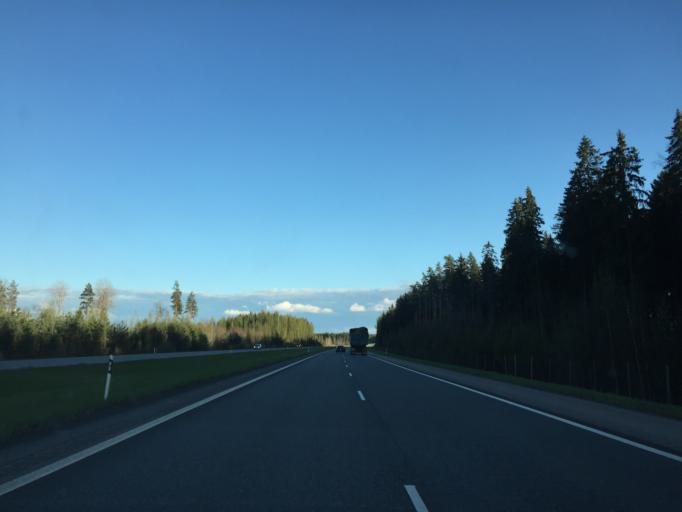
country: FI
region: Haeme
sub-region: Riihimaeki
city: Riihimaeki
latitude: 60.7785
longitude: 24.7100
